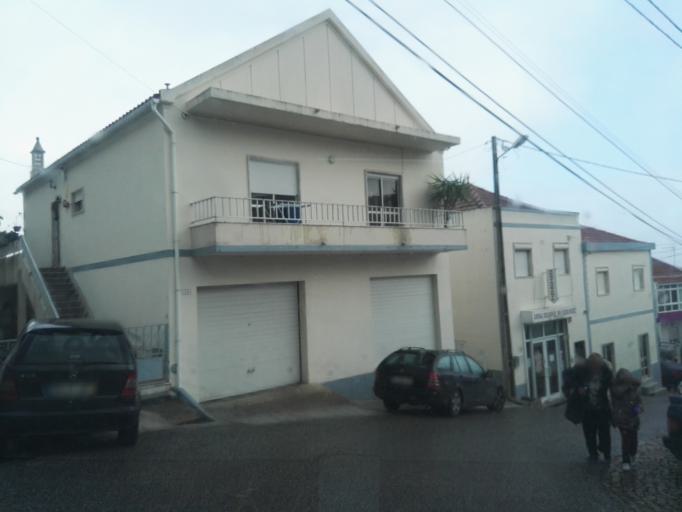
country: PT
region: Lisbon
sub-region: Vila Franca de Xira
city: Sobralinho
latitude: 38.9253
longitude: -9.0681
